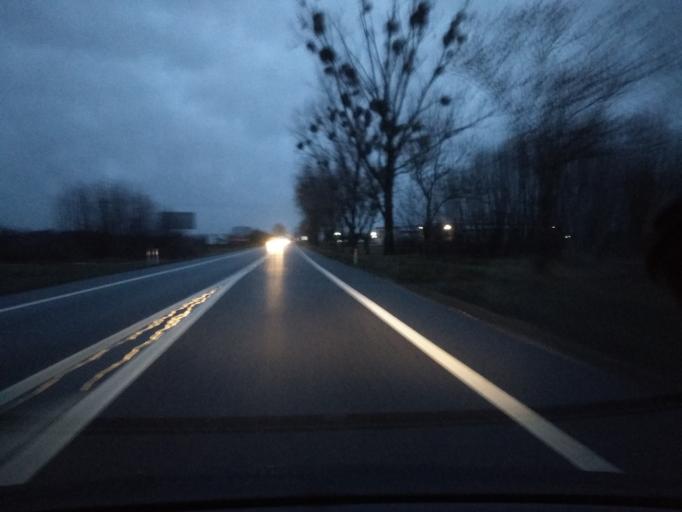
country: PL
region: Lower Silesian Voivodeship
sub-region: Powiat sredzki
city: Mrozow
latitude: 51.1562
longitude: 16.8018
